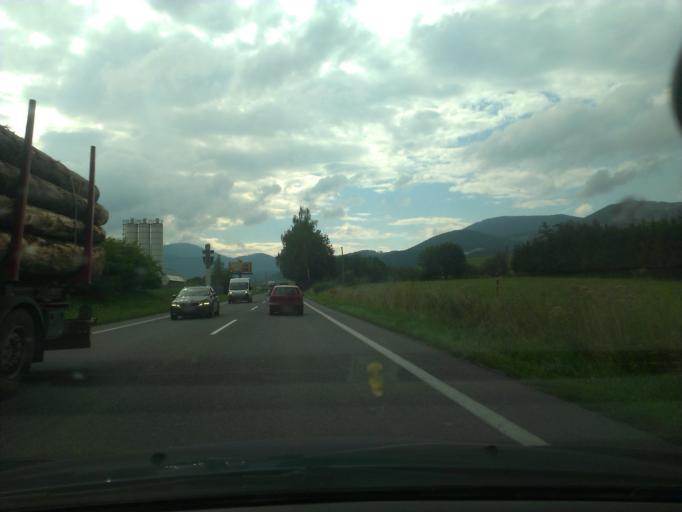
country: SK
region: Zilinsky
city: Krasnany
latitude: 49.1922
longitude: 18.8190
